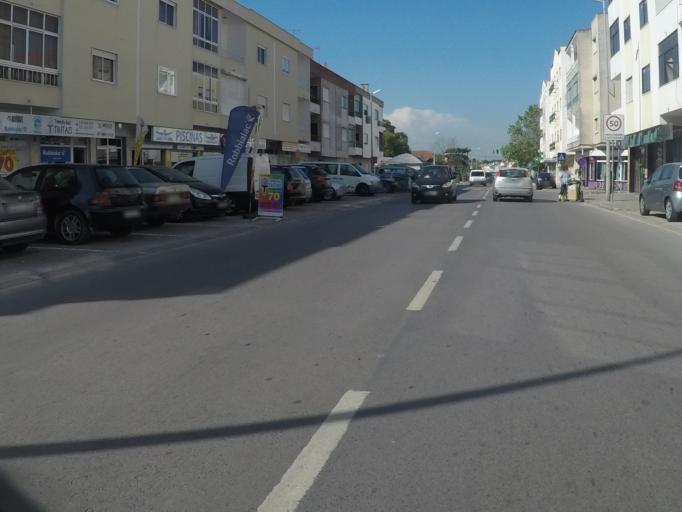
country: PT
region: Setubal
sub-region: Seixal
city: Amora
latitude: 38.6093
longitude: -9.1255
